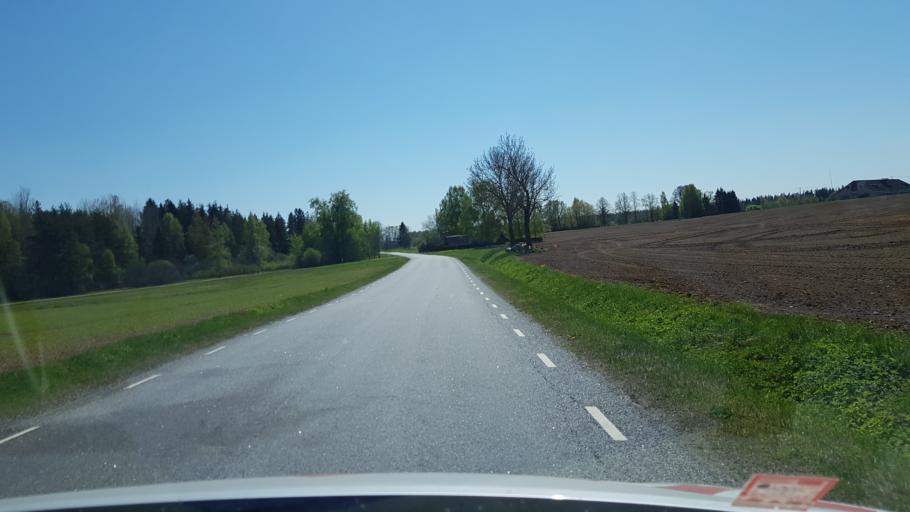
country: EE
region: Vorumaa
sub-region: Voru linn
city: Voru
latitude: 57.9160
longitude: 26.9554
